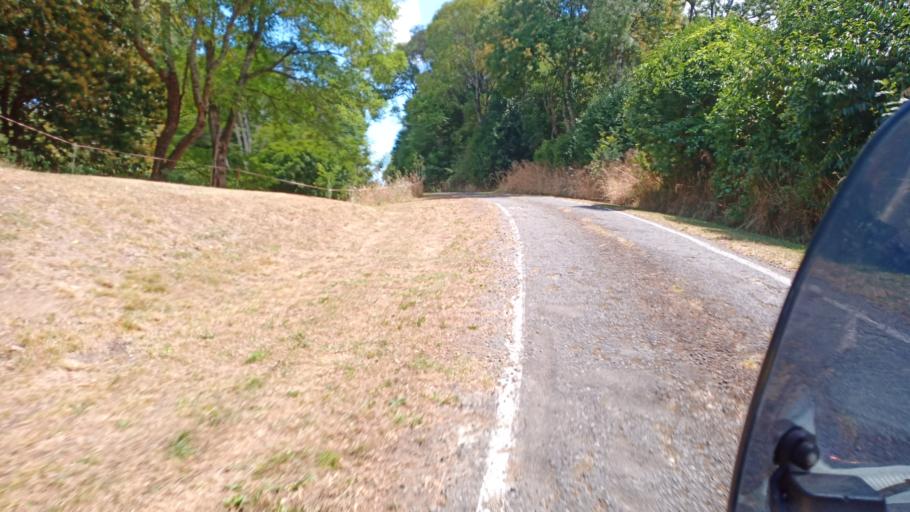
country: NZ
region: Gisborne
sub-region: Gisborne District
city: Gisborne
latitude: -38.4636
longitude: 177.6545
